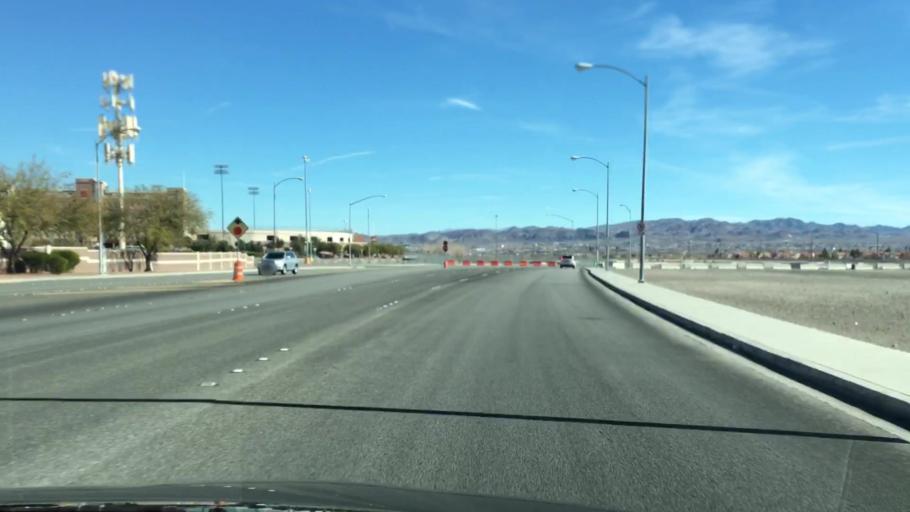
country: US
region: Nevada
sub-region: Clark County
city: Henderson
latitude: 36.0853
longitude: -115.0221
